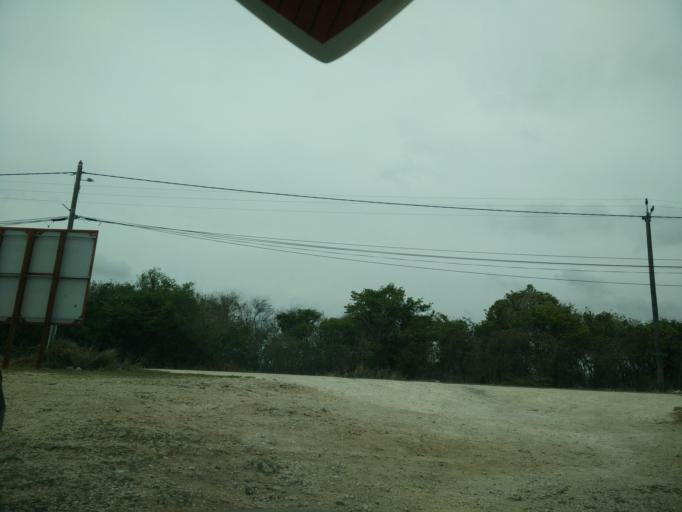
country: GP
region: Guadeloupe
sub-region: Guadeloupe
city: Le Moule
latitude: 16.3240
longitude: -61.3062
